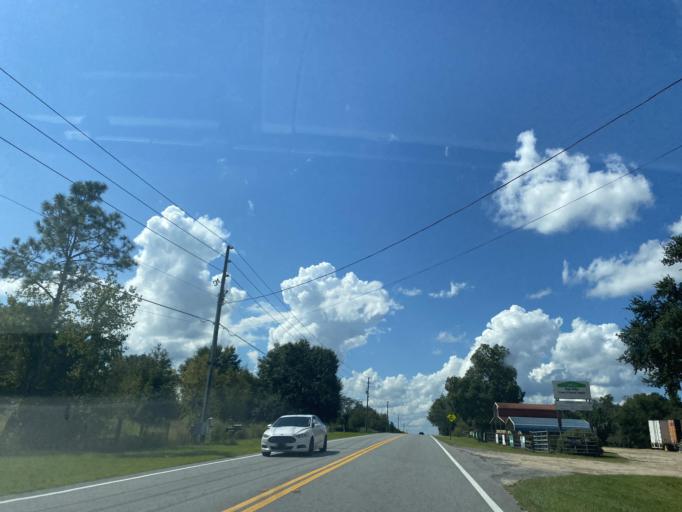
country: US
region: Florida
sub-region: Lake County
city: Lady Lake
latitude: 28.9804
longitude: -81.8773
